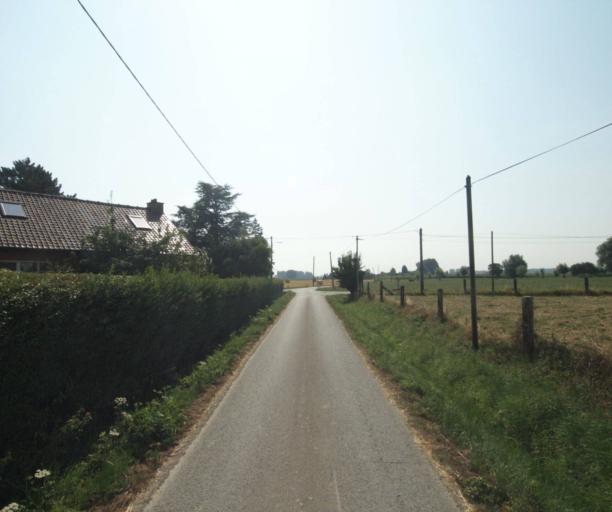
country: FR
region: Nord-Pas-de-Calais
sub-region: Departement du Nord
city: Quesnoy-sur-Deule
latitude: 50.7041
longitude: 2.9771
